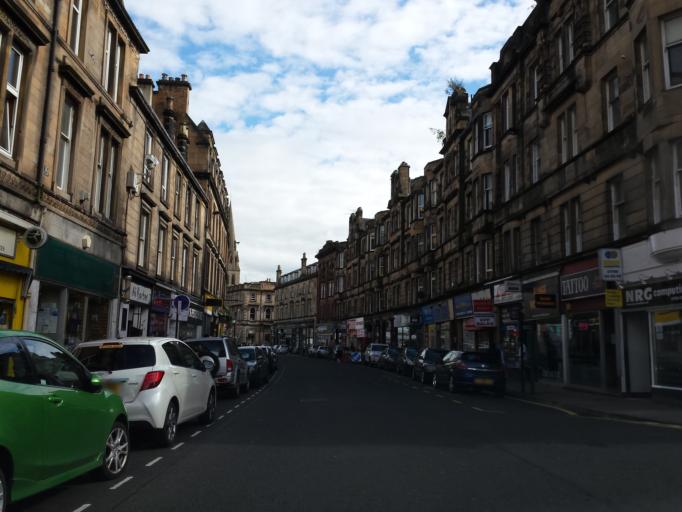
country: GB
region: Scotland
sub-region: Stirling
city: Stirling
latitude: 56.1206
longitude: -3.9384
